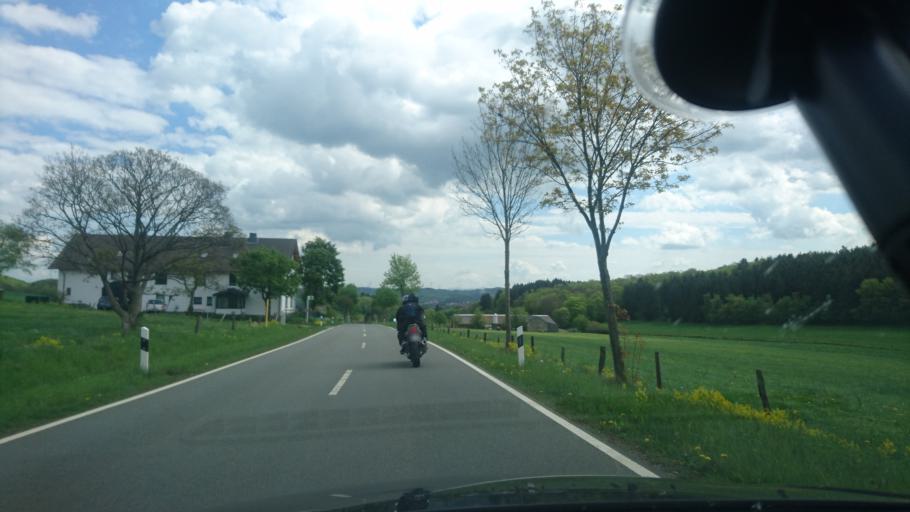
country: DE
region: North Rhine-Westphalia
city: Marsberg
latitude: 51.3576
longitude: 8.7518
